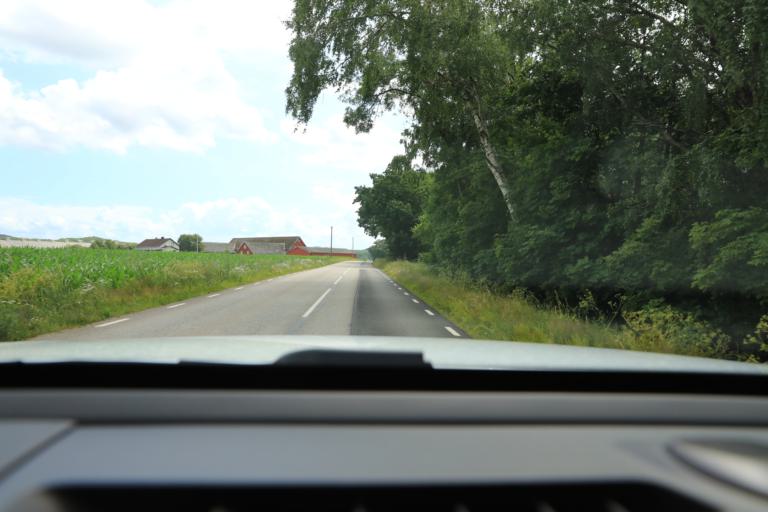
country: SE
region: Halland
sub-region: Varbergs Kommun
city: Tvaaker
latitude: 57.0398
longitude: 12.4361
